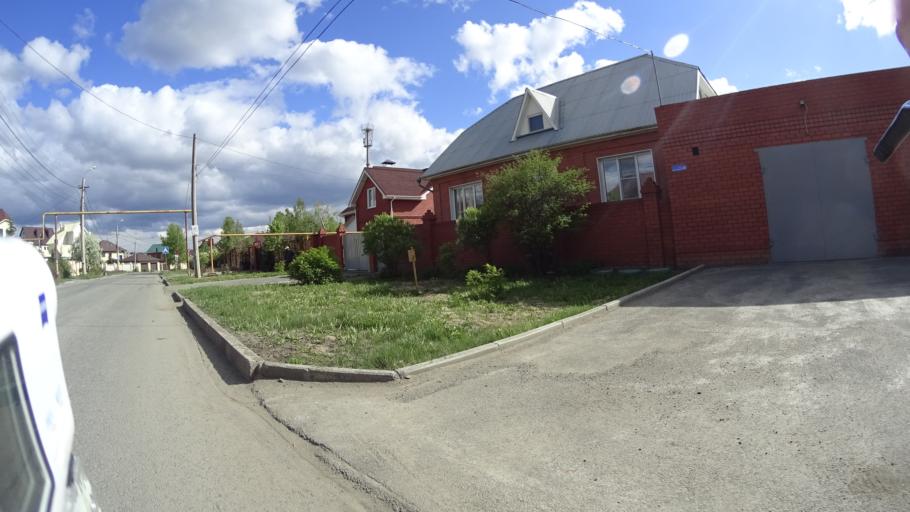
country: RU
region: Chelyabinsk
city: Sargazy
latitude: 55.1550
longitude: 61.2532
